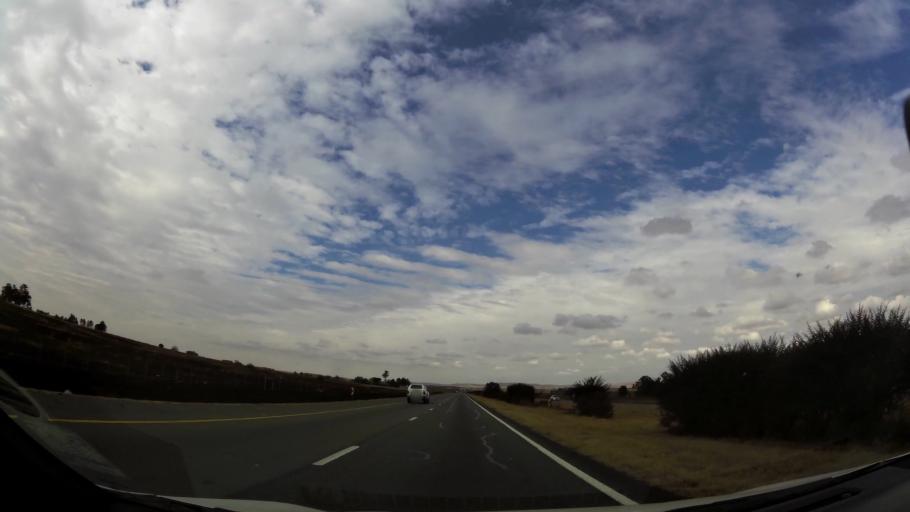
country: ZA
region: Gauteng
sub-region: Ekurhuleni Metropolitan Municipality
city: Germiston
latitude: -26.3613
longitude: 28.2351
